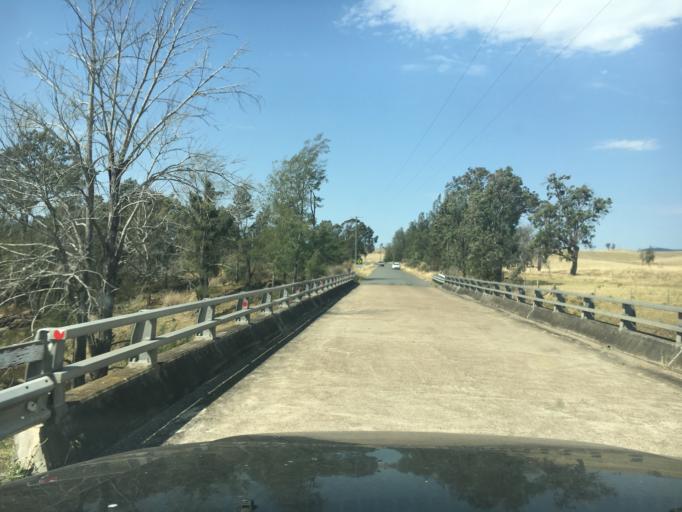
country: AU
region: New South Wales
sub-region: Singleton
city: Singleton
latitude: -32.5086
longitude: 151.2790
